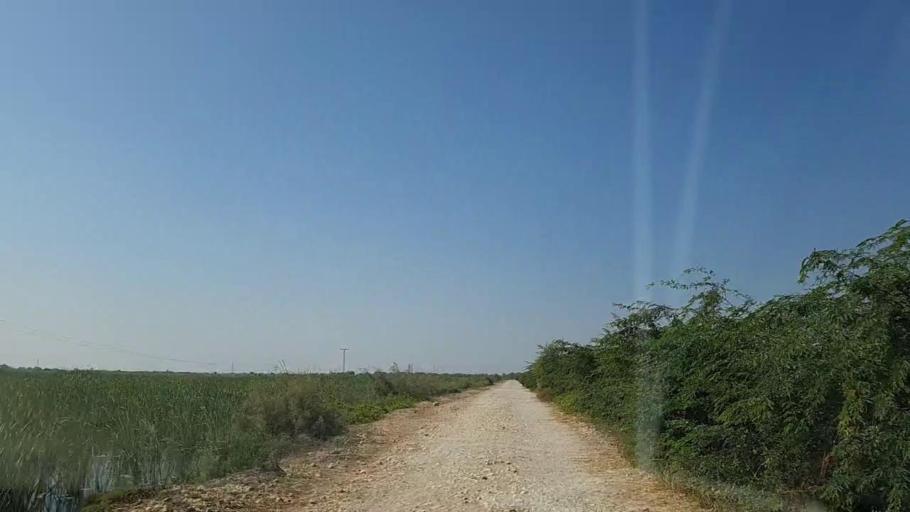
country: PK
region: Sindh
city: Chuhar Jamali
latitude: 24.4154
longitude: 68.0371
